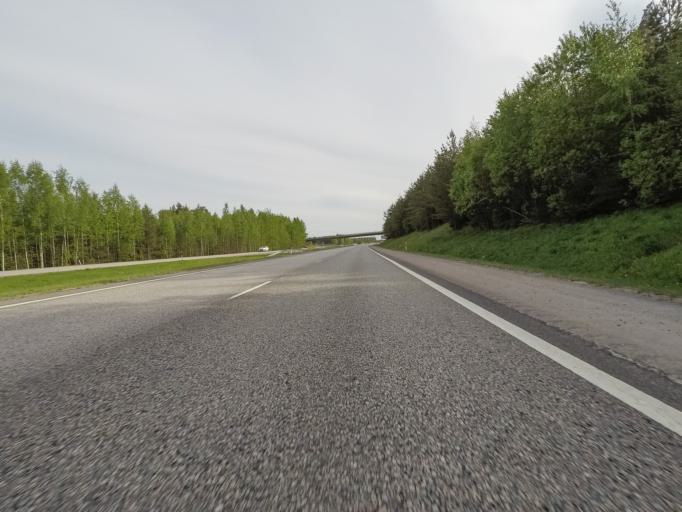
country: FI
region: Uusimaa
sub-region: Helsinki
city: Nurmijaervi
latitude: 60.4646
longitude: 24.8492
